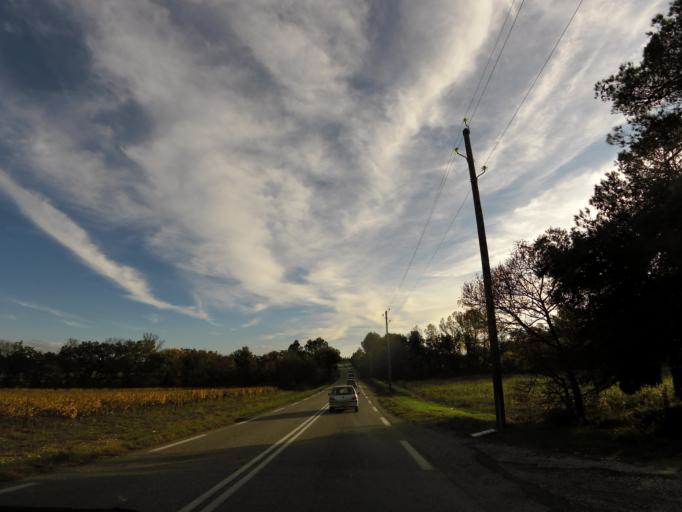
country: FR
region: Languedoc-Roussillon
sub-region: Departement du Gard
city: Ledignan
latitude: 43.9650
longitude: 4.0981
